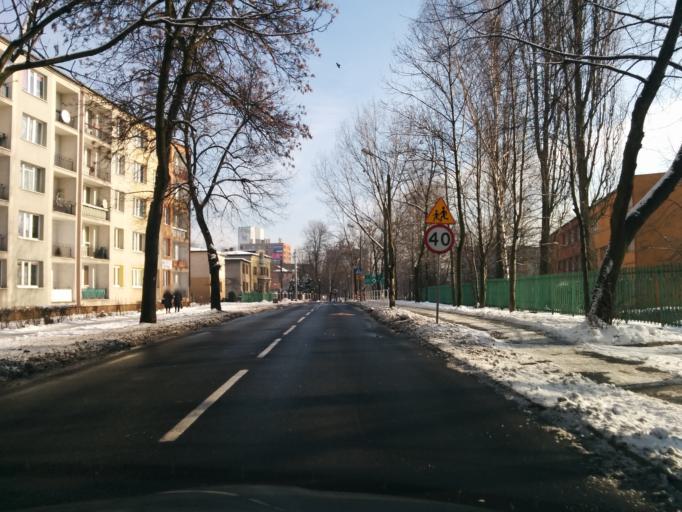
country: PL
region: Silesian Voivodeship
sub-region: Ruda Slaska
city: Ruda Slaska
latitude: 50.2764
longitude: 18.8588
